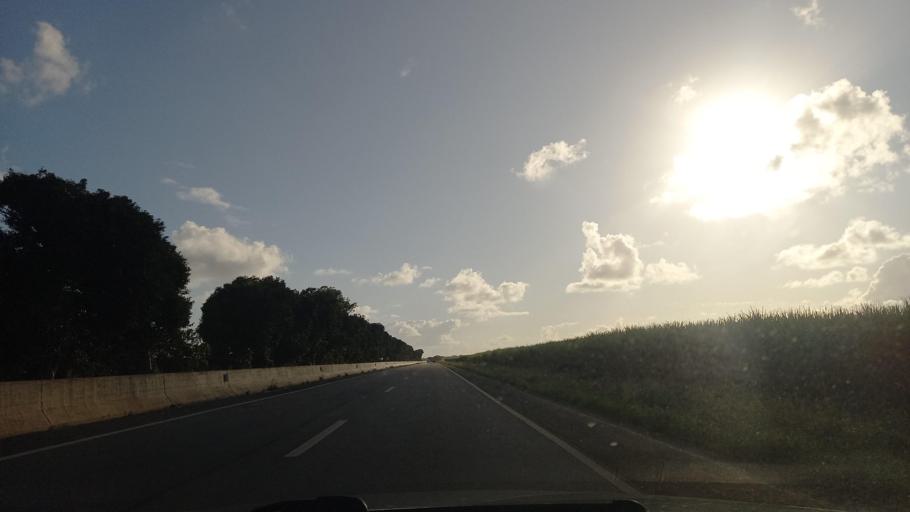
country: BR
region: Alagoas
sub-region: Sao Miguel Dos Campos
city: Sao Miguel dos Campos
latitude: -9.7998
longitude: -36.1729
